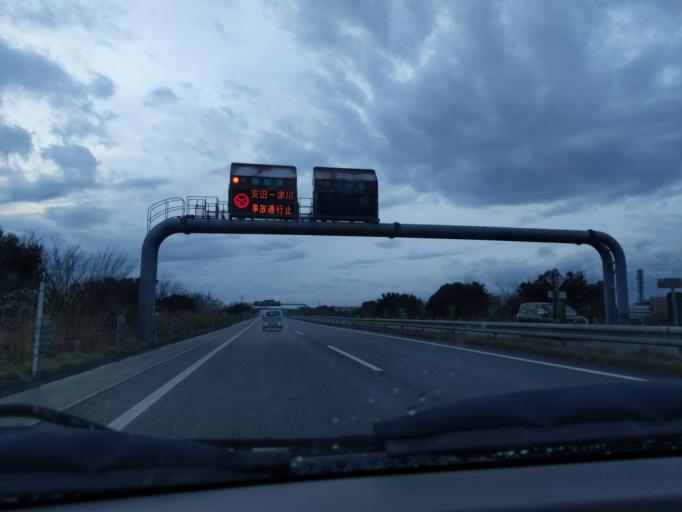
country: JP
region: Niigata
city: Niigata-shi
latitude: 37.8744
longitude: 139.0541
